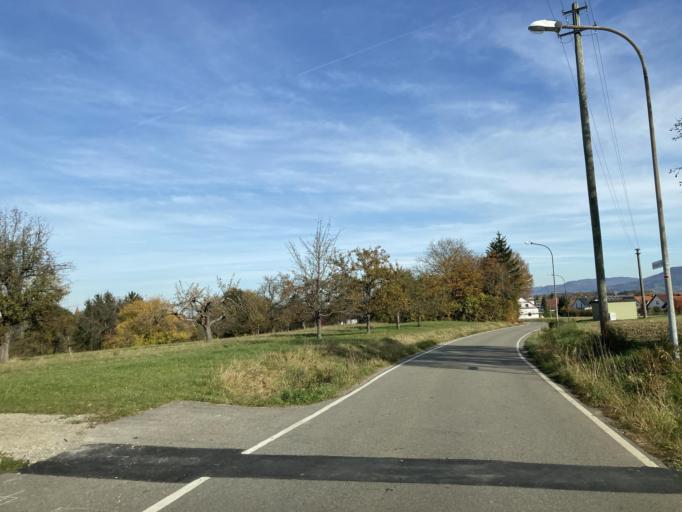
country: DE
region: Baden-Wuerttemberg
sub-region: Tuebingen Region
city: Bodelshausen
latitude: 48.3914
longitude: 8.9618
